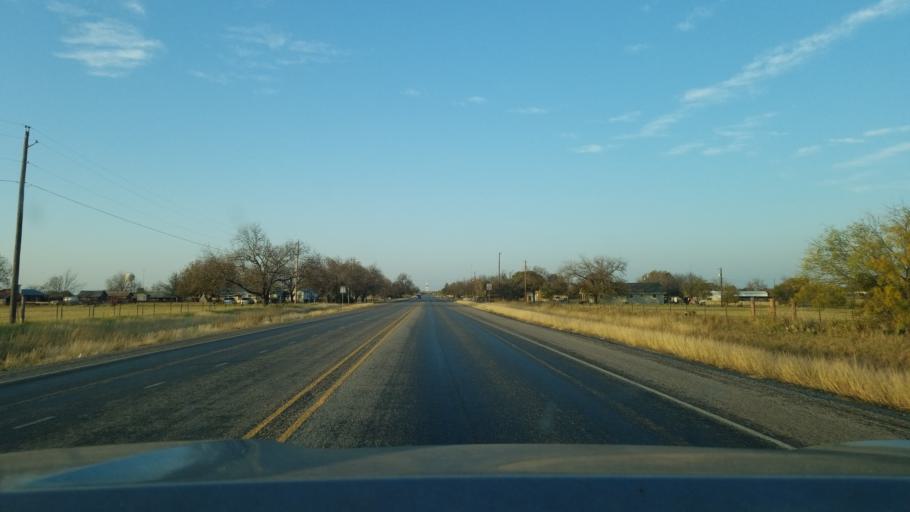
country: US
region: Texas
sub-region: Eastland County
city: Cisco
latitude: 32.3634
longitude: -98.9700
